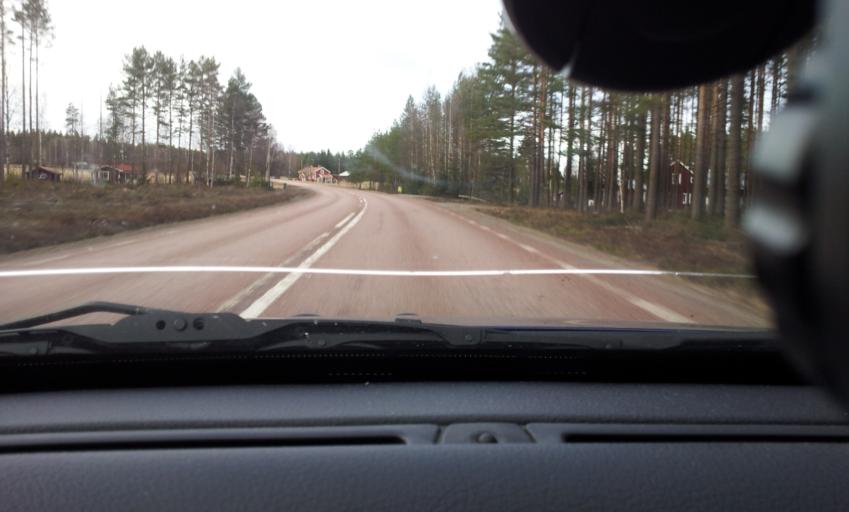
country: SE
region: Gaevleborg
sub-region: Ljusdals Kommun
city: Farila
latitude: 61.8357
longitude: 15.7510
